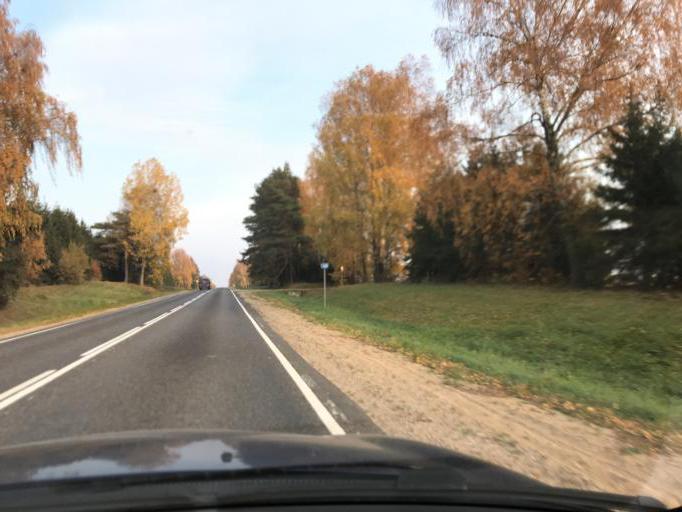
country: BY
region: Grodnenskaya
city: Karelichy
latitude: 53.5938
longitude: 26.0082
